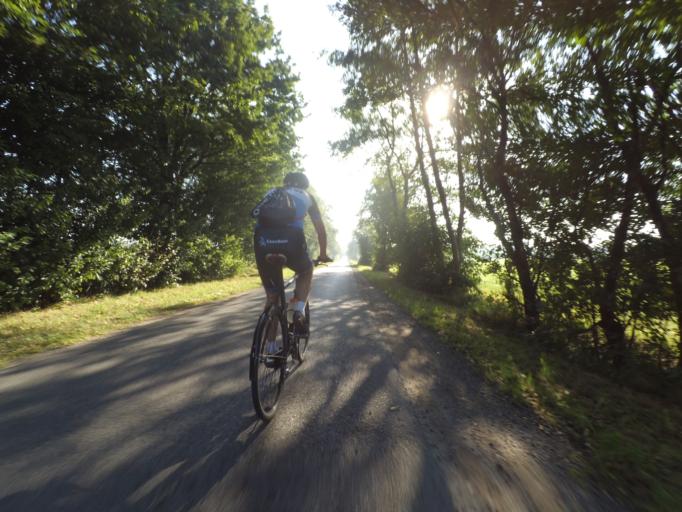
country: DE
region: Lower Saxony
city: Suddendorf
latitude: 52.2769
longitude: 7.2362
